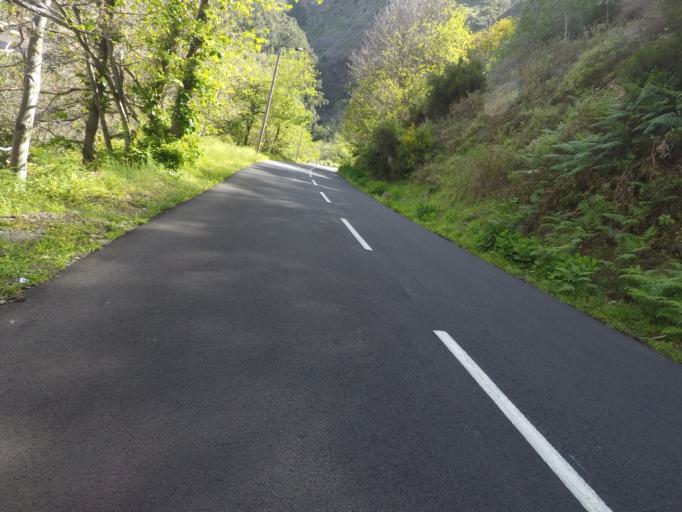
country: PT
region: Madeira
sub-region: Camara de Lobos
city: Curral das Freiras
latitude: 32.7169
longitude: -16.9641
